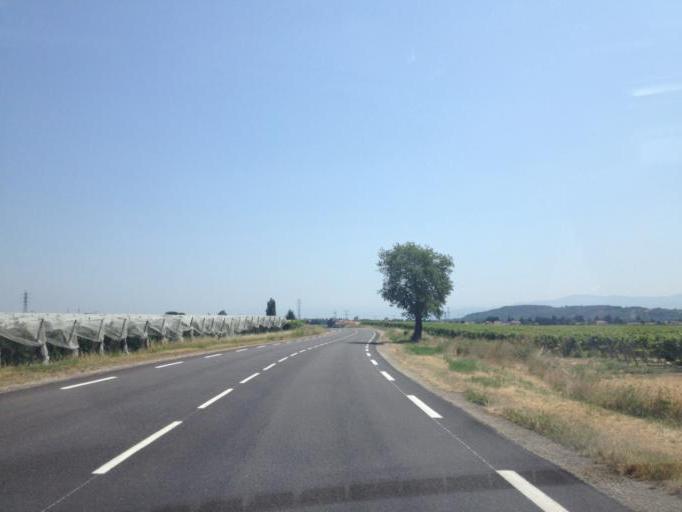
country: FR
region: Rhone-Alpes
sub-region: Departement de la Drome
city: Beaumont-Monteux
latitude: 45.0224
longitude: 4.9027
